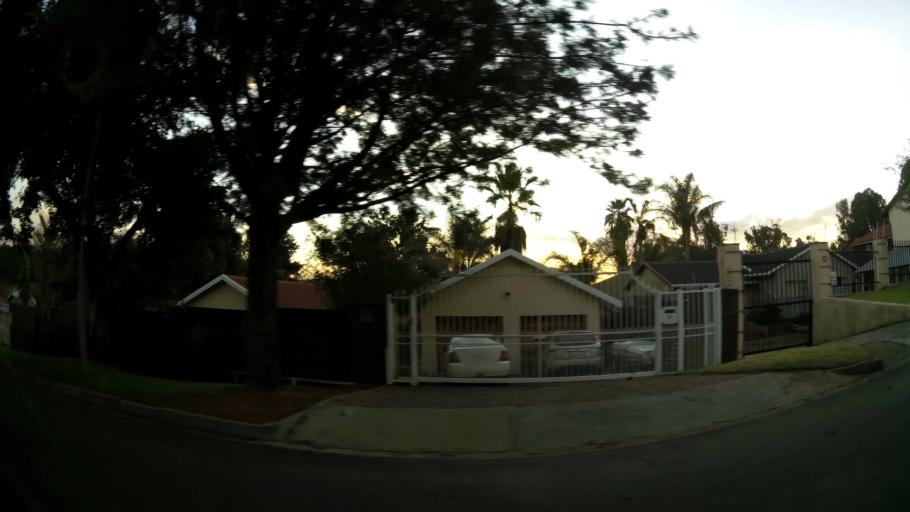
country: ZA
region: Gauteng
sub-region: West Rand District Municipality
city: Krugersdorp
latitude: -26.0727
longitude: 27.7806
